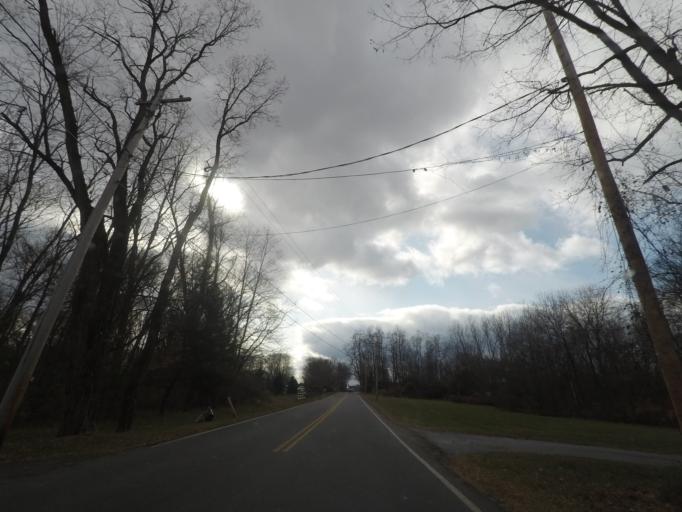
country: US
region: New York
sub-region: Saratoga County
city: Ballston Spa
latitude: 42.9897
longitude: -73.8177
